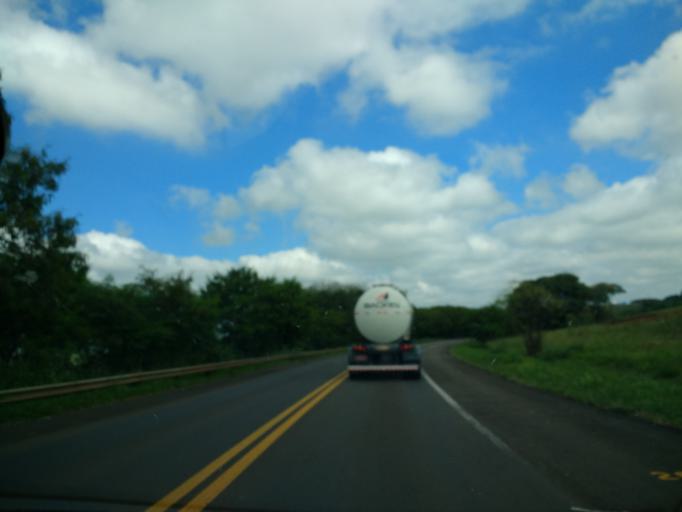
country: BR
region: Parana
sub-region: Cruzeiro Do Oeste
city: Cruzeiro do Oeste
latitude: -23.7874
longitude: -53.0274
